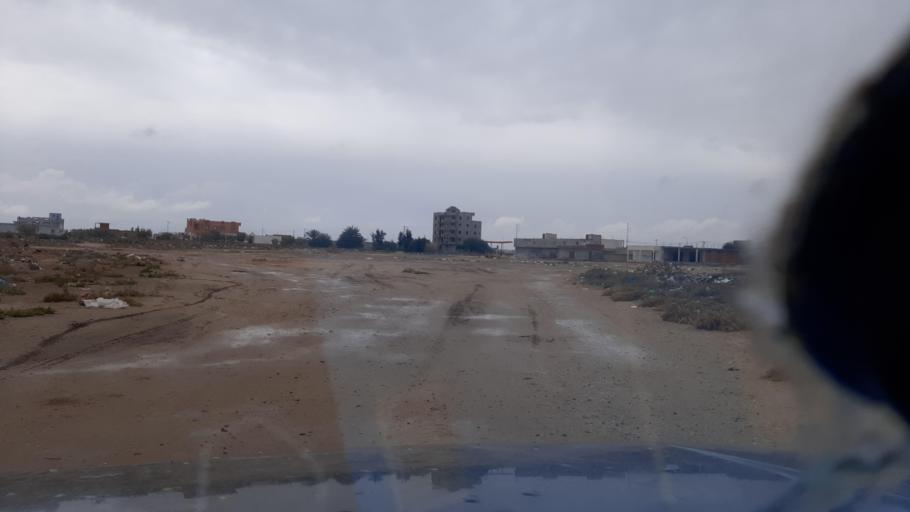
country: TN
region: Al Mahdiyah
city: Shurban
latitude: 35.4359
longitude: 10.3961
